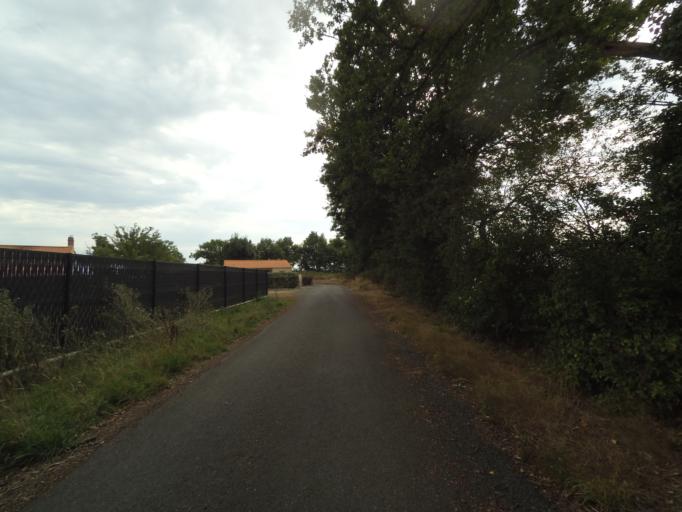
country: FR
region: Pays de la Loire
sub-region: Departement de la Vendee
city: Bouffere
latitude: 46.9701
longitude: -1.3676
